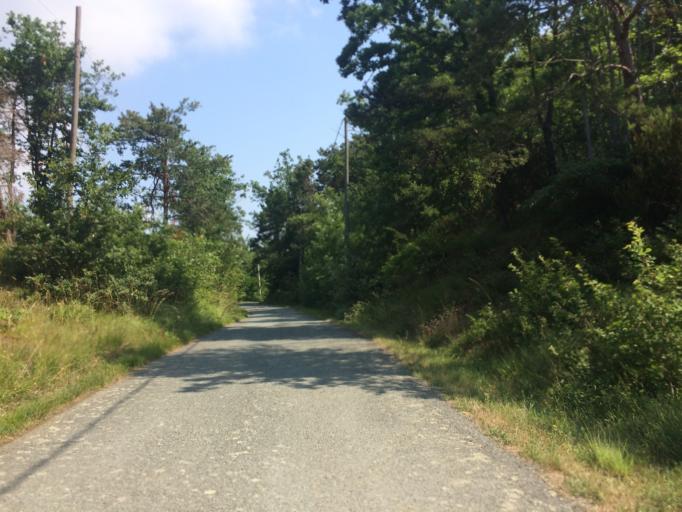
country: IT
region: Piedmont
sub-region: Provincia di Alessandria
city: Pareto
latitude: 44.5033
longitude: 8.3752
